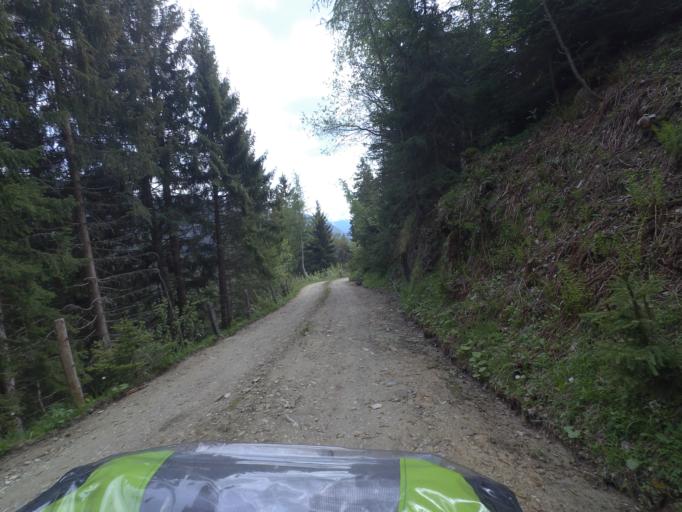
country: AT
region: Salzburg
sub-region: Politischer Bezirk Sankt Johann im Pongau
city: Dorfgastein
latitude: 47.2585
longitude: 13.1241
